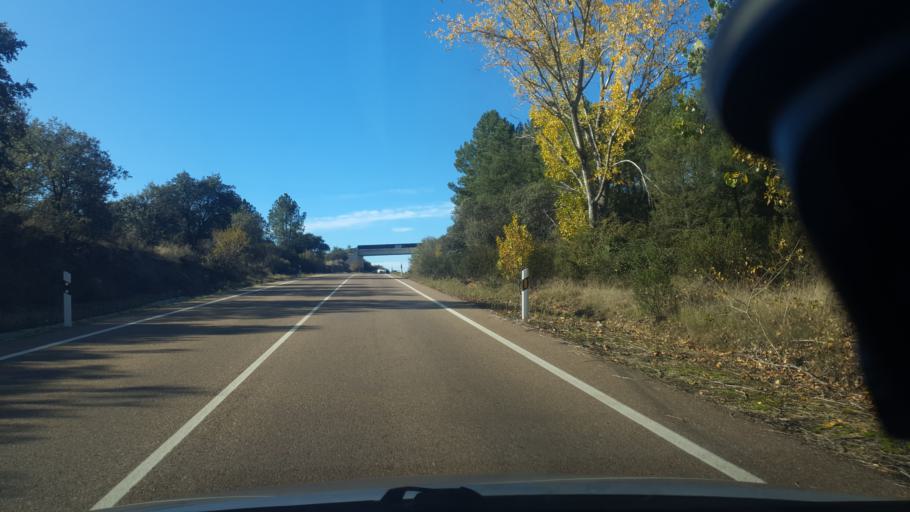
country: ES
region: Castille and Leon
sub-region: Provincia de Avila
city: Arenas de San Pedro
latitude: 40.1642
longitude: -5.1077
